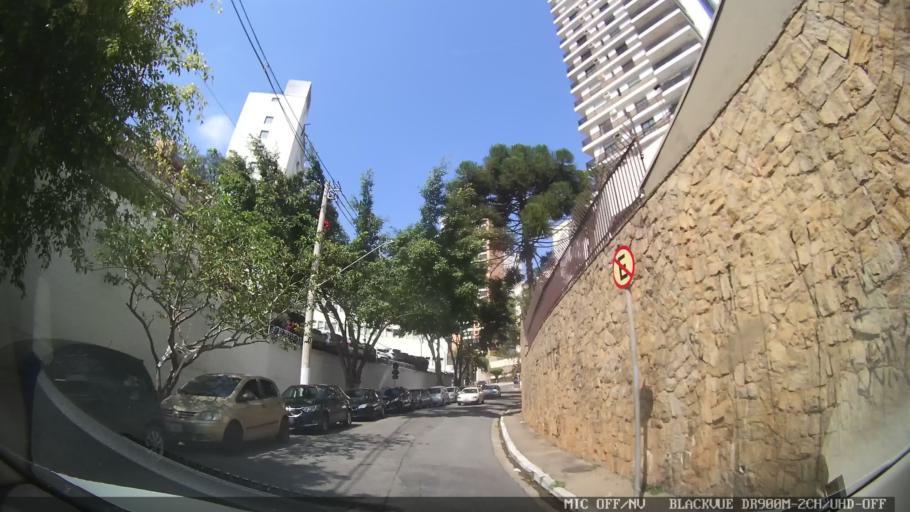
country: BR
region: Sao Paulo
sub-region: Sao Paulo
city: Sao Paulo
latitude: -23.4877
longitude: -46.6282
